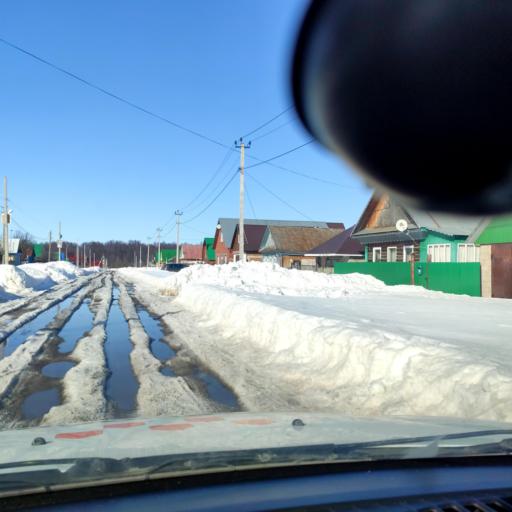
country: RU
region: Bashkortostan
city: Mikhaylovka
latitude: 54.8419
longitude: 55.8349
